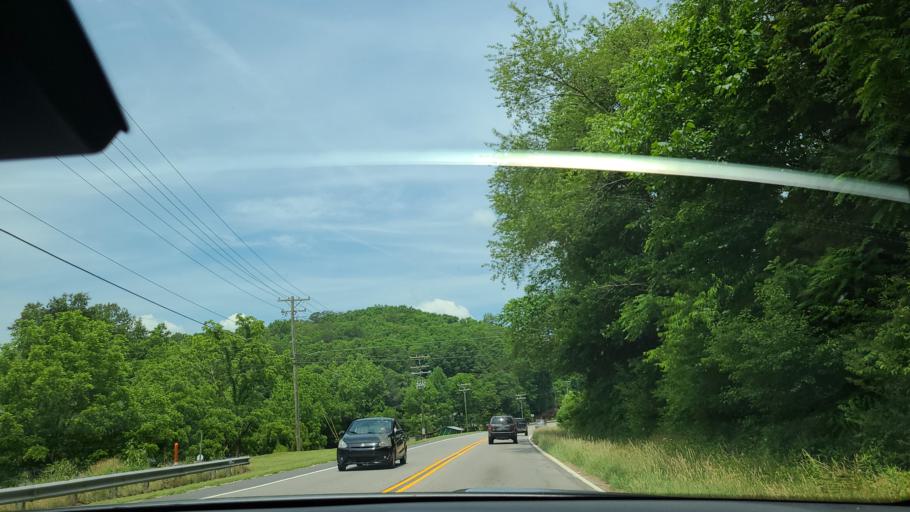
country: US
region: North Carolina
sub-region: Macon County
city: Franklin
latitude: 35.1699
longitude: -83.3383
